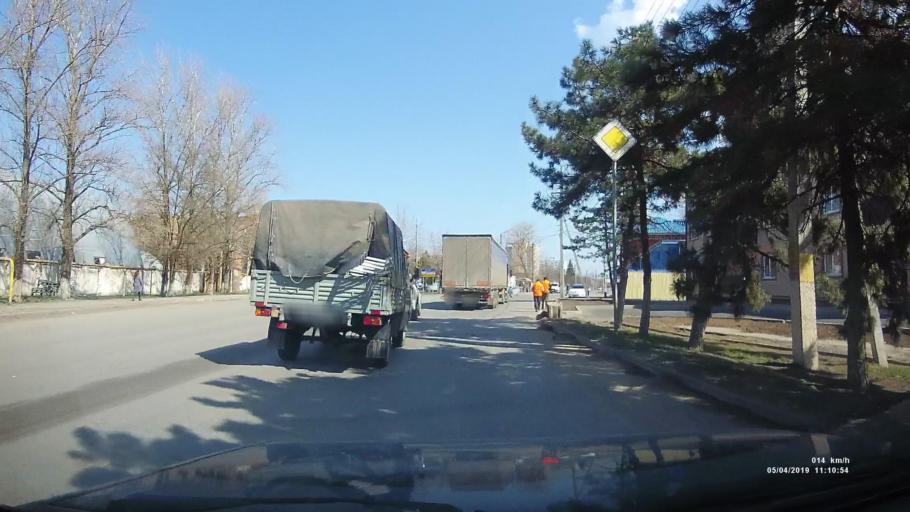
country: RU
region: Rostov
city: Azov
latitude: 47.0931
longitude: 39.4324
